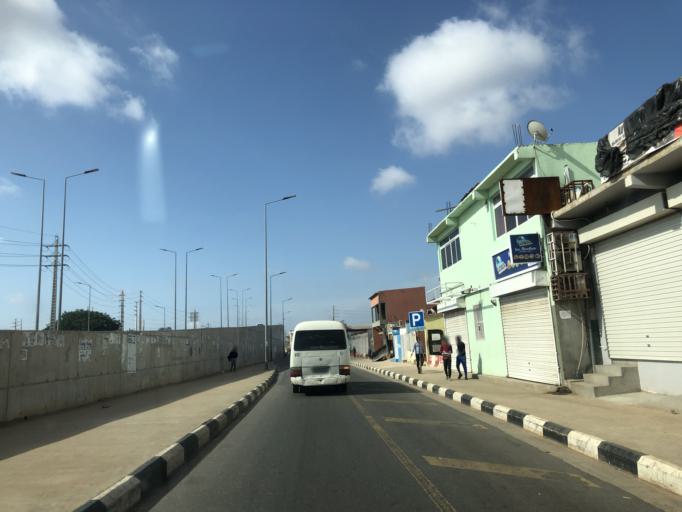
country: AO
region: Luanda
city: Luanda
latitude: -8.9039
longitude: 13.2612
